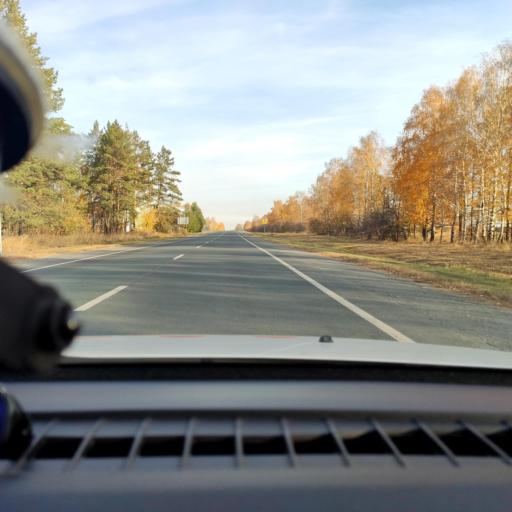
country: RU
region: Samara
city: Volzhskiy
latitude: 53.4530
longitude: 50.1261
